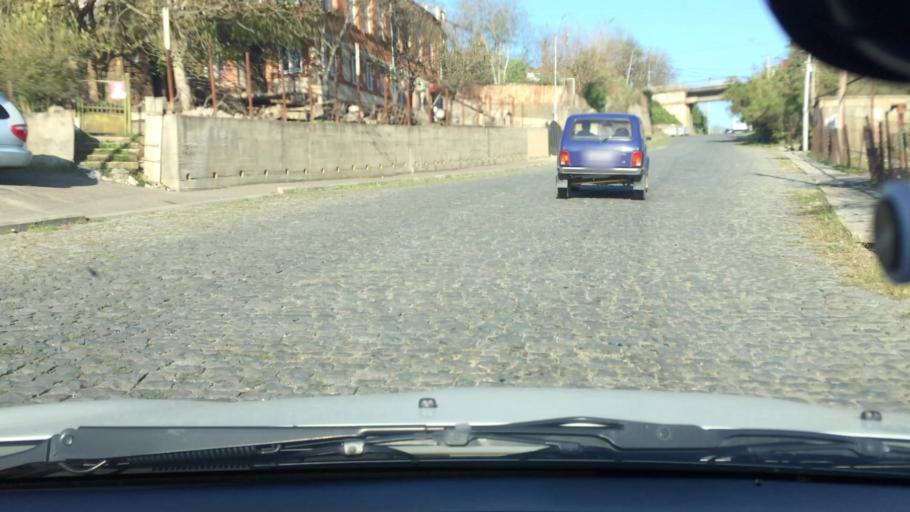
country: GE
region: Imereti
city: Kutaisi
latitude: 42.2647
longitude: 42.7203
